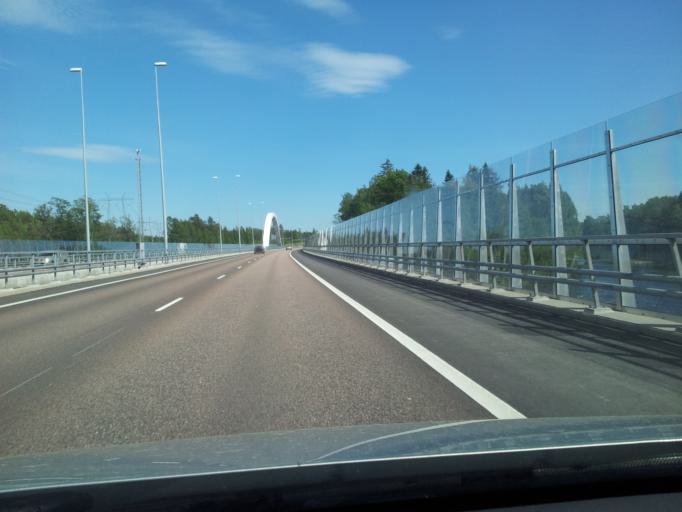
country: FI
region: Uusimaa
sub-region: Loviisa
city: Ruotsinpyhtaeae
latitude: 60.4922
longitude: 26.4470
